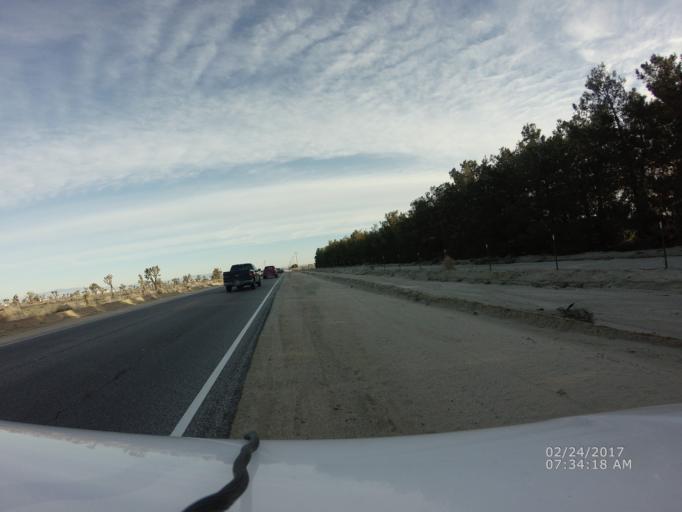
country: US
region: California
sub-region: Los Angeles County
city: Palmdale
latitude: 34.6058
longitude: -118.0409
